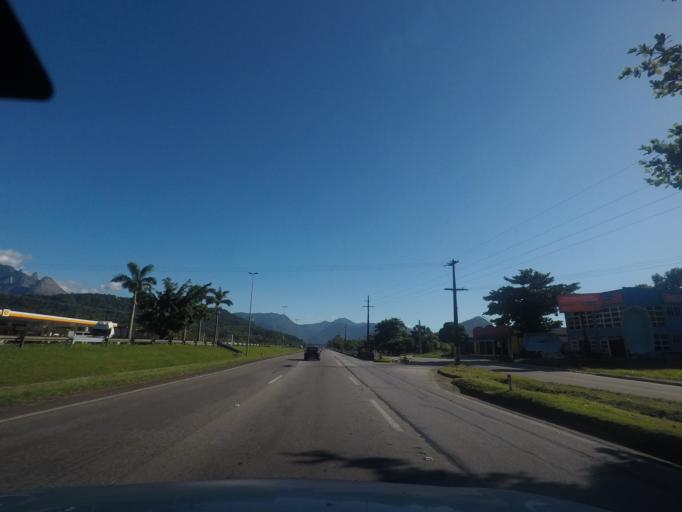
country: BR
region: Rio de Janeiro
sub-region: Guapimirim
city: Guapimirim
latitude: -22.5644
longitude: -42.9993
